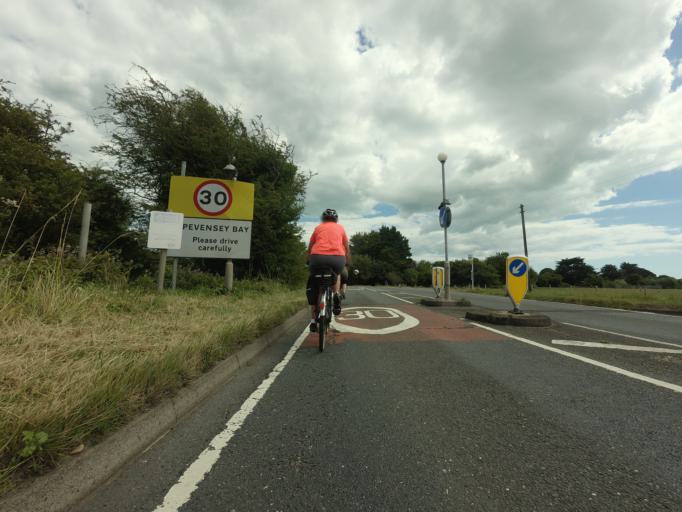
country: GB
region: England
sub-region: East Sussex
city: Pevensey
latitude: 50.8155
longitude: 0.3490
